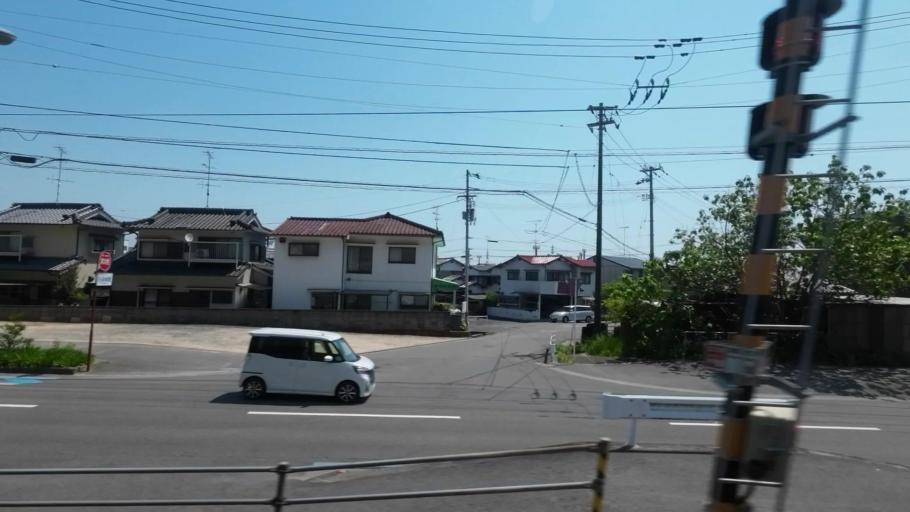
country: JP
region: Ehime
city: Hojo
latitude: 34.0776
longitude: 132.9853
